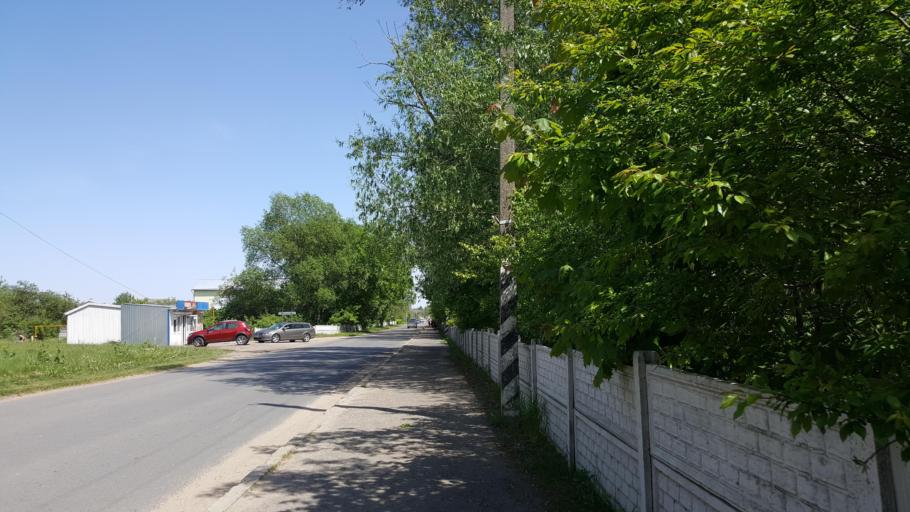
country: BY
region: Brest
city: Brest
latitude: 52.1574
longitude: 23.6420
